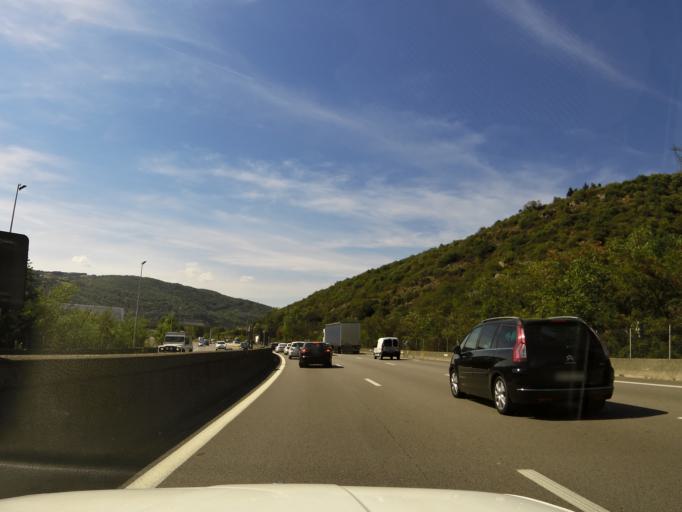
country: FR
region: Rhone-Alpes
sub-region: Departement du Rhone
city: Saint-Romain-en-Gal
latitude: 45.5433
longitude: 4.8519
